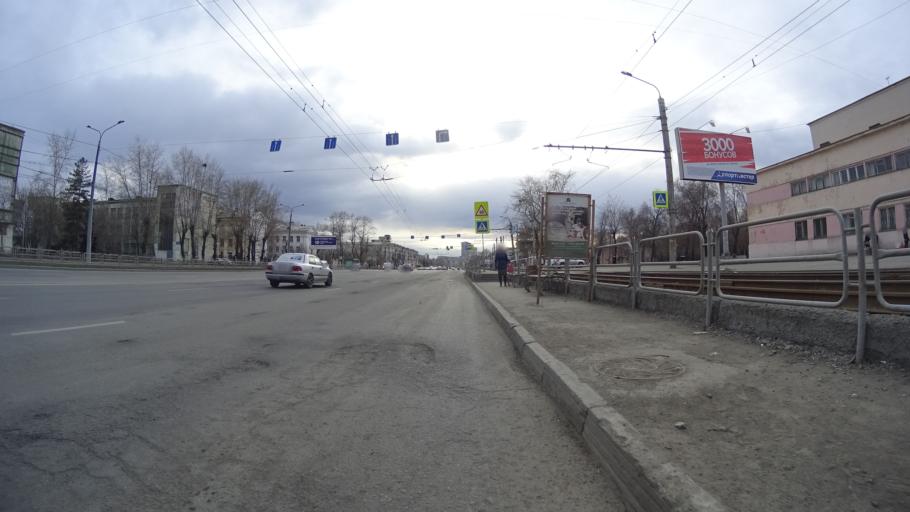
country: RU
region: Chelyabinsk
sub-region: Gorod Chelyabinsk
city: Chelyabinsk
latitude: 55.1601
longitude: 61.4537
